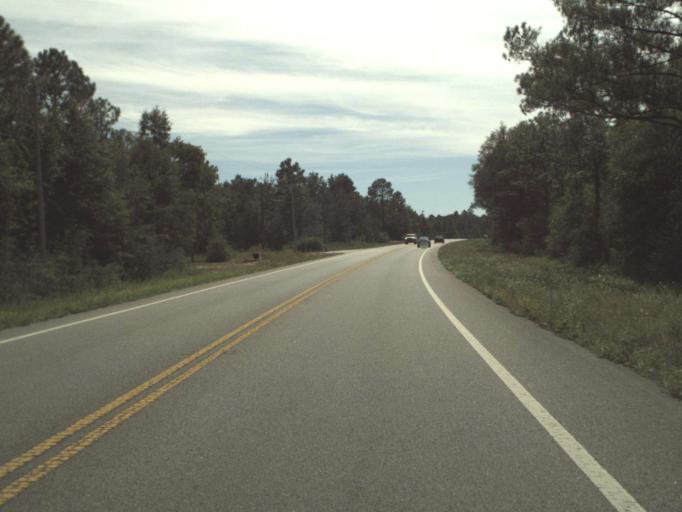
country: US
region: Florida
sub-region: Washington County
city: Chipley
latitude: 30.5896
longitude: -85.5919
